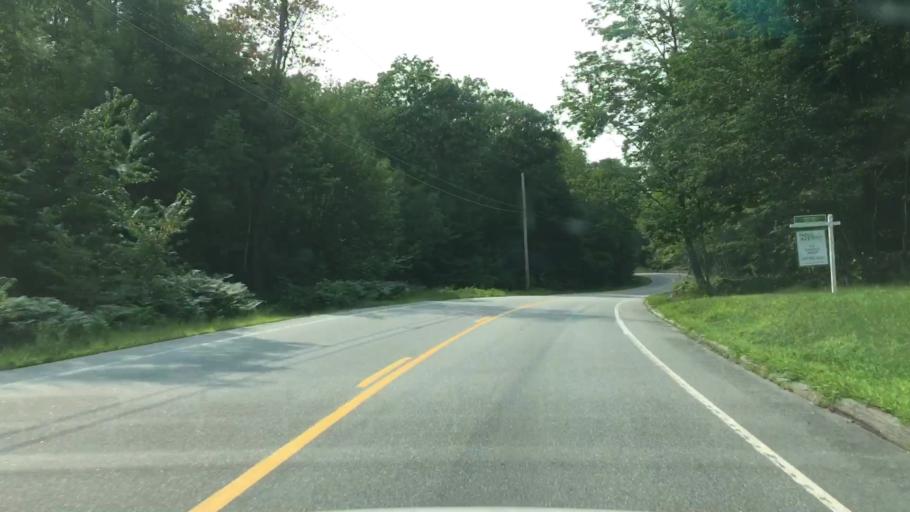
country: US
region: Maine
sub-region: Oxford County
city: Buckfield
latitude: 44.2709
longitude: -70.3984
